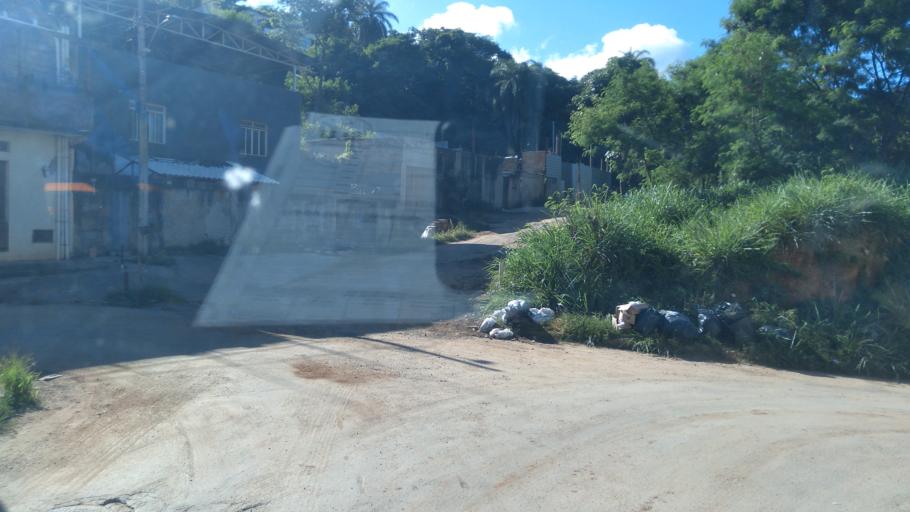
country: BR
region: Minas Gerais
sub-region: Belo Horizonte
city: Belo Horizonte
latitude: -19.9210
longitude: -43.8977
